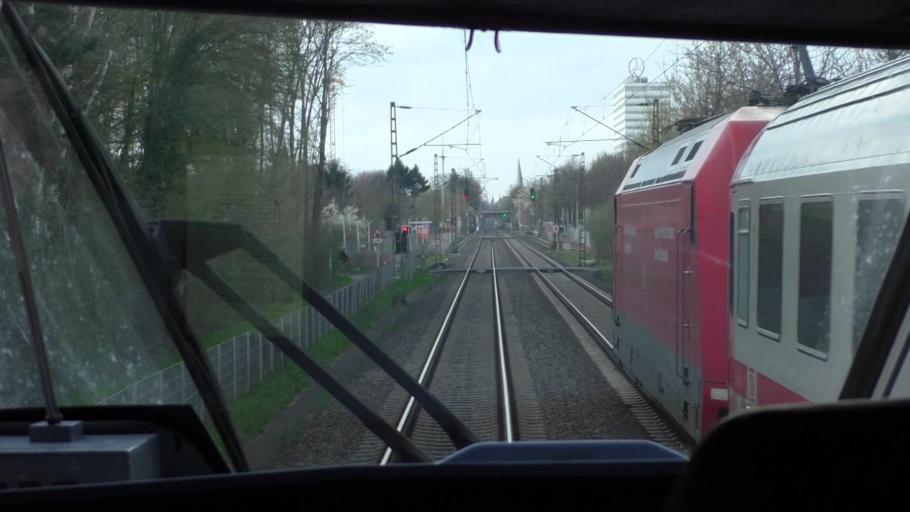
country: DE
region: North Rhine-Westphalia
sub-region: Regierungsbezirk Koln
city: Bonn
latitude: 50.7114
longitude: 7.1211
